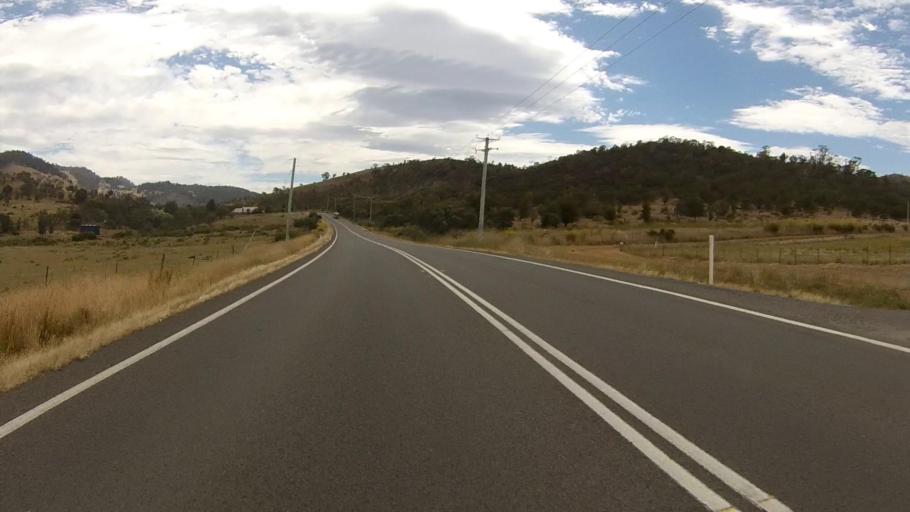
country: AU
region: Tasmania
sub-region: Brighton
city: Old Beach
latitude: -42.6881
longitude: 147.3511
